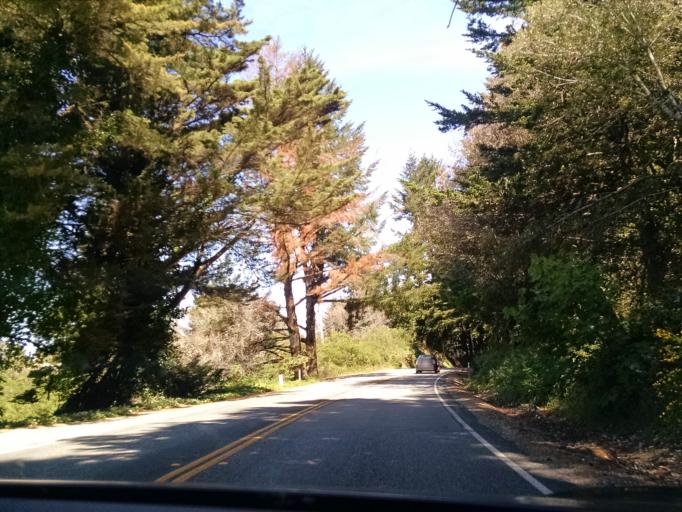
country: US
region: California
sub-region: San Mateo County
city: Highlands-Baywood Park
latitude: 37.4548
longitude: -122.3406
